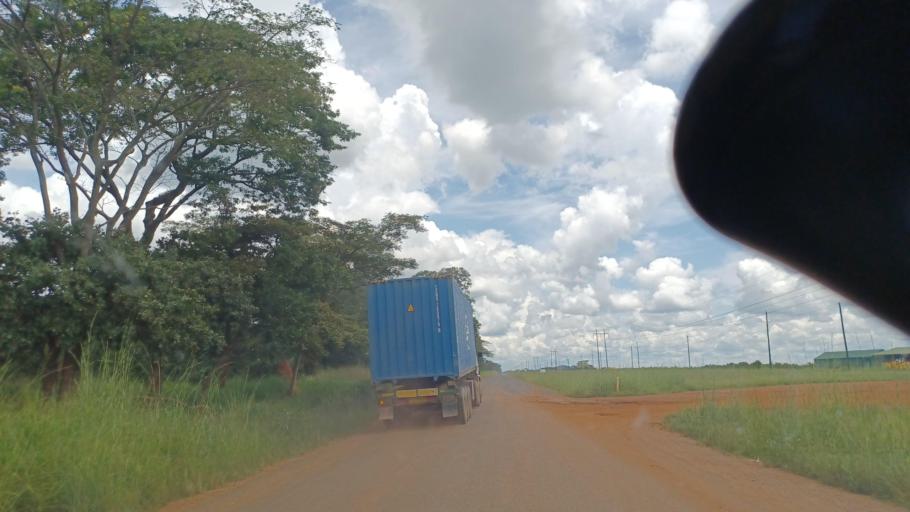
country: ZM
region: North-Western
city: Solwezi
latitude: -12.4382
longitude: 26.2098
